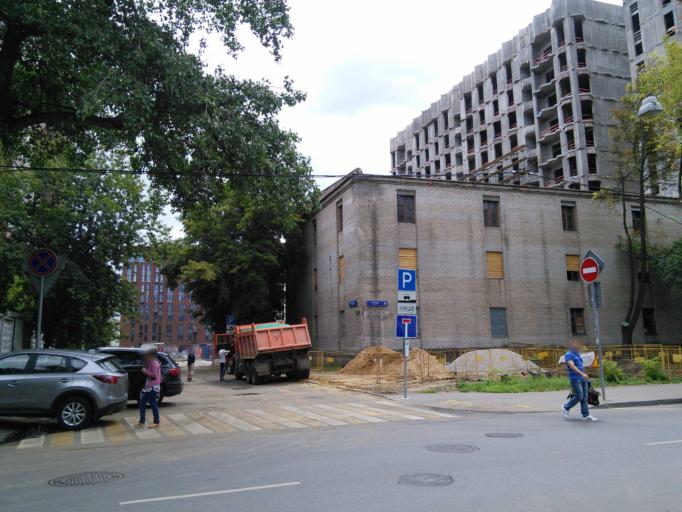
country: RU
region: Moskovskaya
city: Dorogomilovo
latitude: 55.7288
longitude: 37.5723
